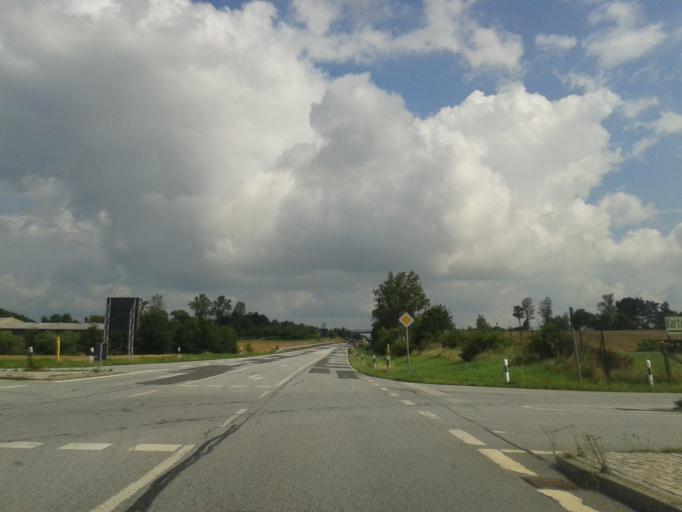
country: DE
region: Saxony
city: Goda
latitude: 51.1973
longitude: 14.3652
